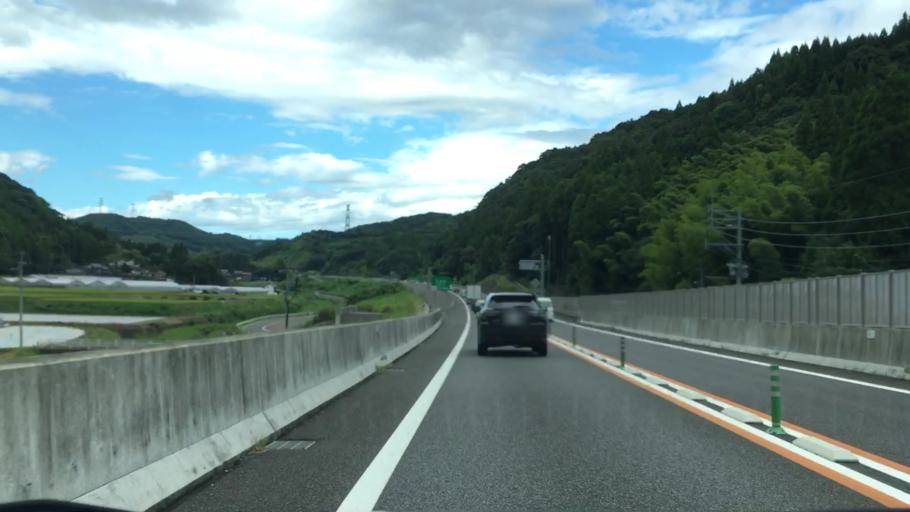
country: JP
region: Saga Prefecture
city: Karatsu
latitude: 33.3766
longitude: 129.9322
